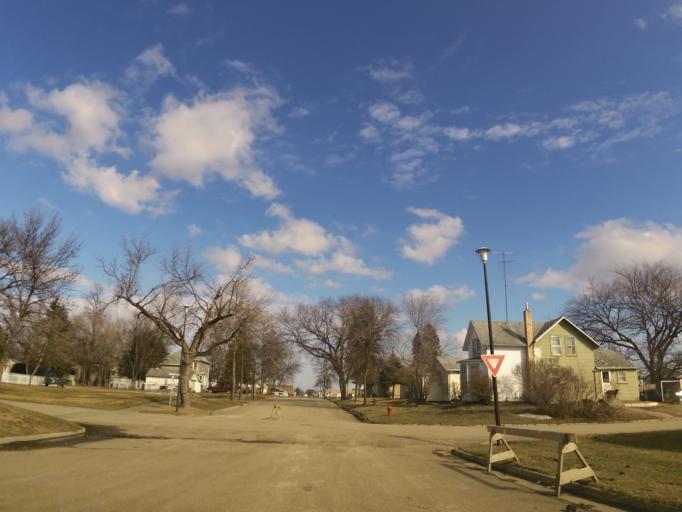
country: US
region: North Dakota
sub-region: Walsh County
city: Grafton
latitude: 48.4206
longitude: -97.4161
